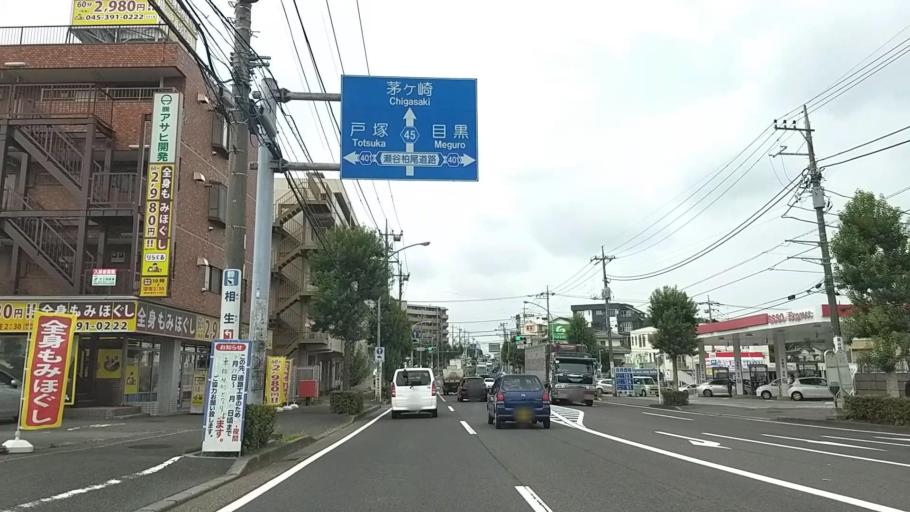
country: JP
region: Kanagawa
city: Minami-rinkan
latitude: 35.4688
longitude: 139.4944
